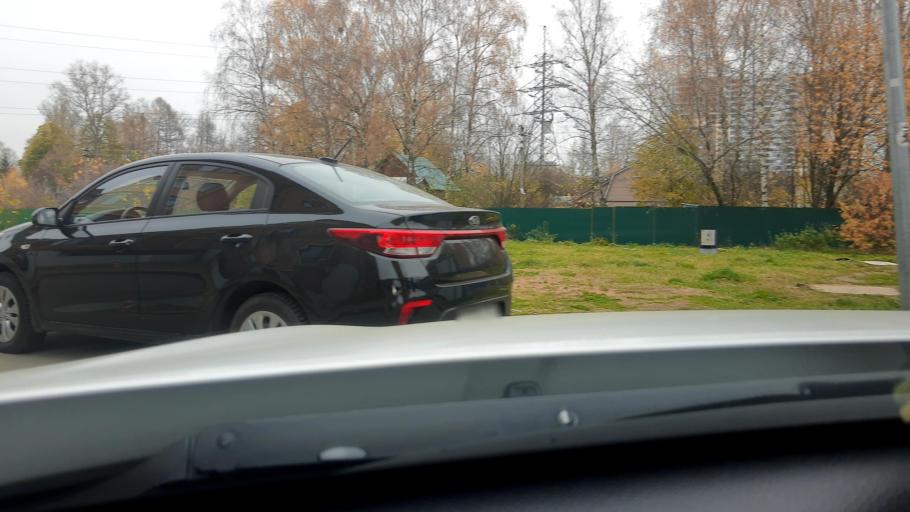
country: RU
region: Moskovskaya
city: Dolgoprudnyy
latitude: 55.9499
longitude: 37.4767
